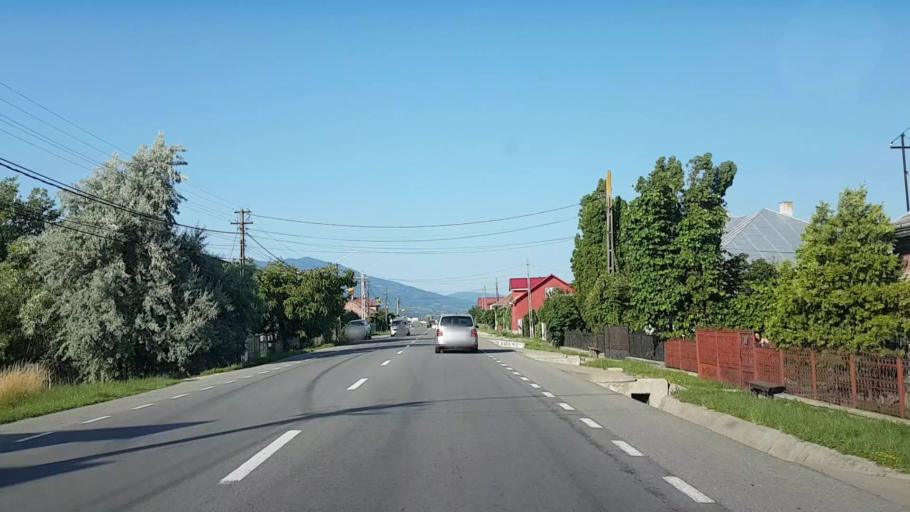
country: RO
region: Bistrita-Nasaud
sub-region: Comuna Josenii Bargaului
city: Josenii Bargaului
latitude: 47.2016
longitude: 24.6441
